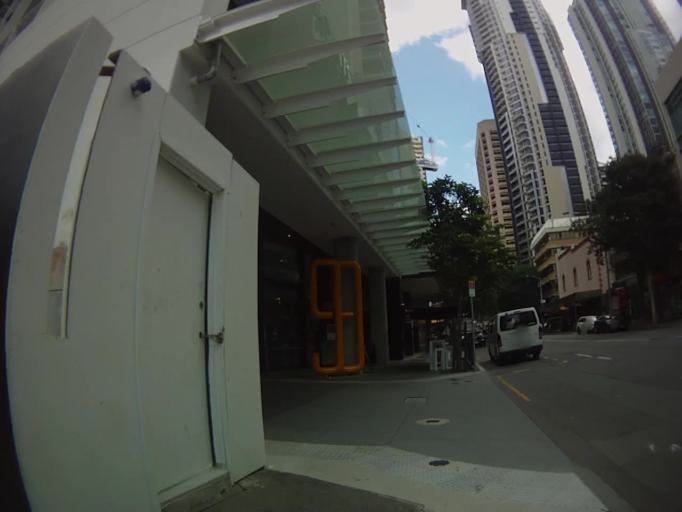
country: AU
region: Queensland
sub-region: Brisbane
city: Brisbane
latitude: -27.4716
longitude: 153.0281
